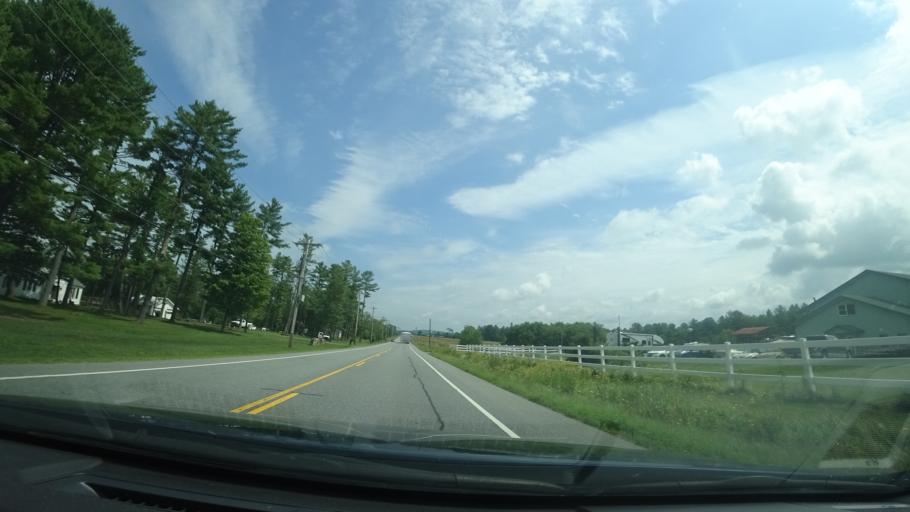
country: US
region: New York
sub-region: Warren County
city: Queensbury
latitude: 43.3775
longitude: -73.5104
